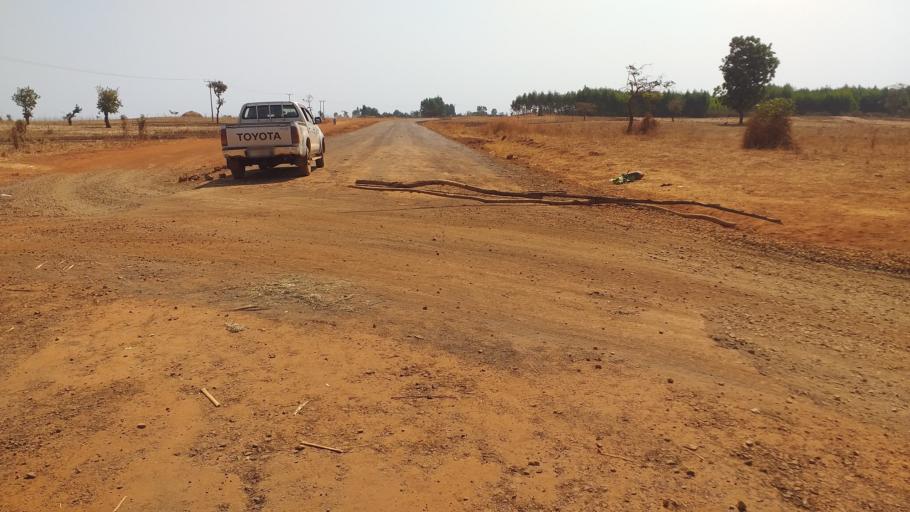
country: ET
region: Binshangul Gumuz
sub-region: Asosa
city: Asosa
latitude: 10.0801
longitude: 34.6516
